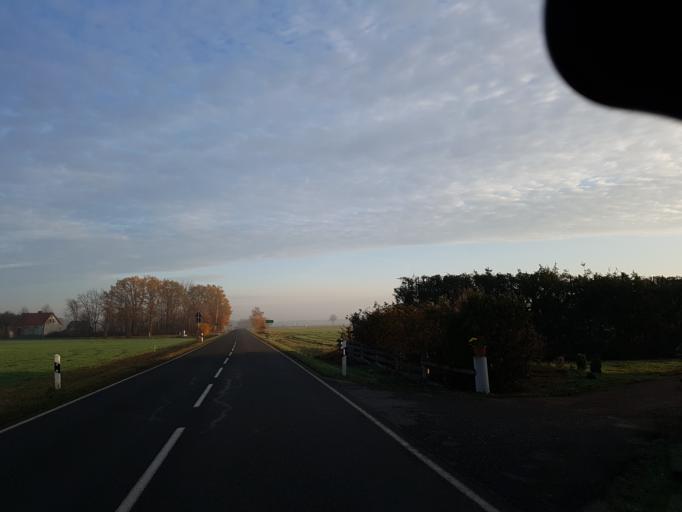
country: DE
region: Saxony-Anhalt
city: Elster
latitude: 51.8456
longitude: 12.8386
